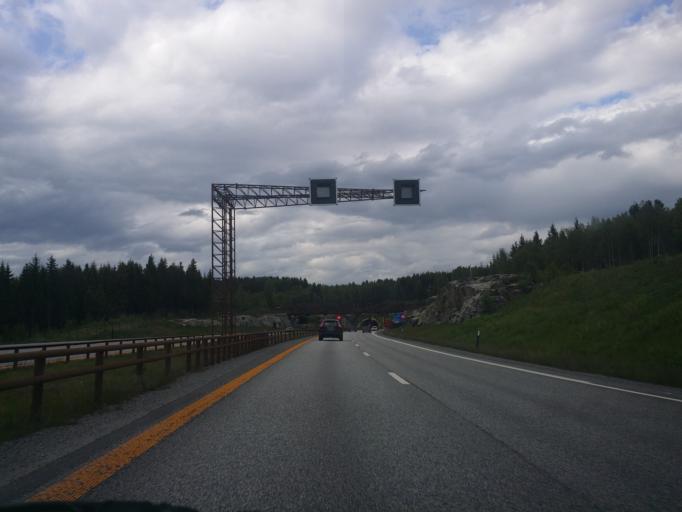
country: NO
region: Akershus
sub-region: Eidsvoll
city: Raholt
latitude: 60.3340
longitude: 11.1923
